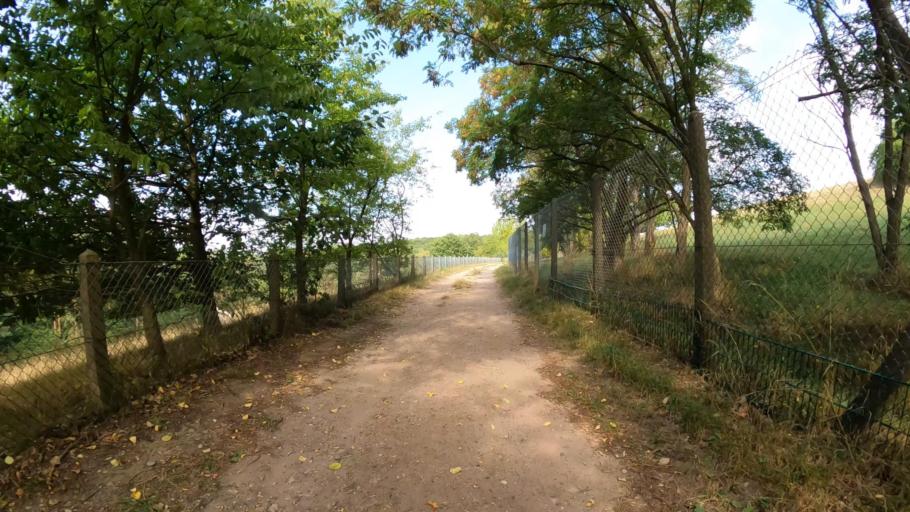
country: DE
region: Lower Saxony
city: Marschacht
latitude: 53.4220
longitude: 10.4002
